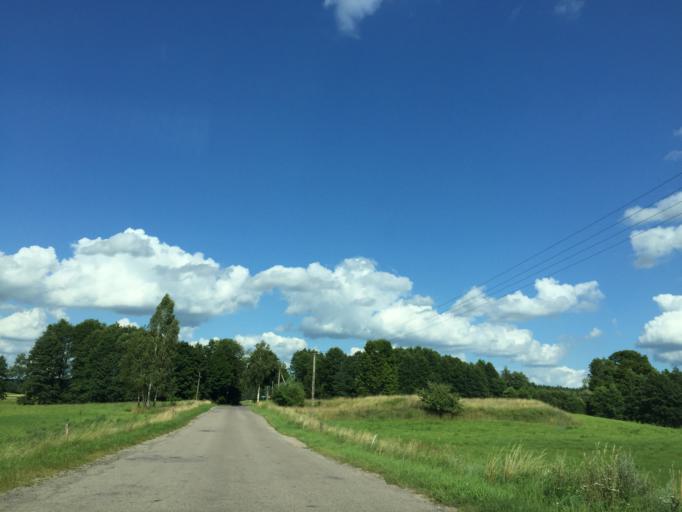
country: PL
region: Podlasie
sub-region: Suwalki
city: Suwalki
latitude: 54.1446
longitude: 23.0543
